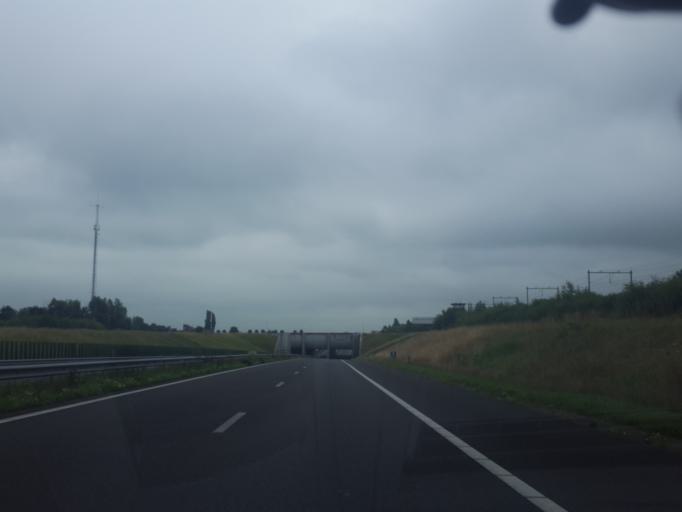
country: NL
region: Friesland
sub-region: Gemeente Boarnsterhim
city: Grou
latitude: 53.0826
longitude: 5.8270
